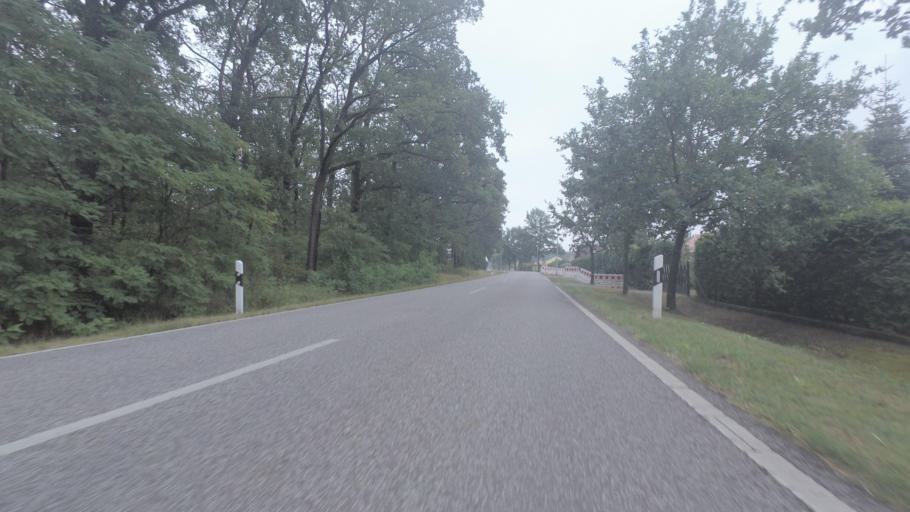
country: DE
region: Brandenburg
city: Paulinenaue
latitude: 52.6686
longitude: 12.7195
